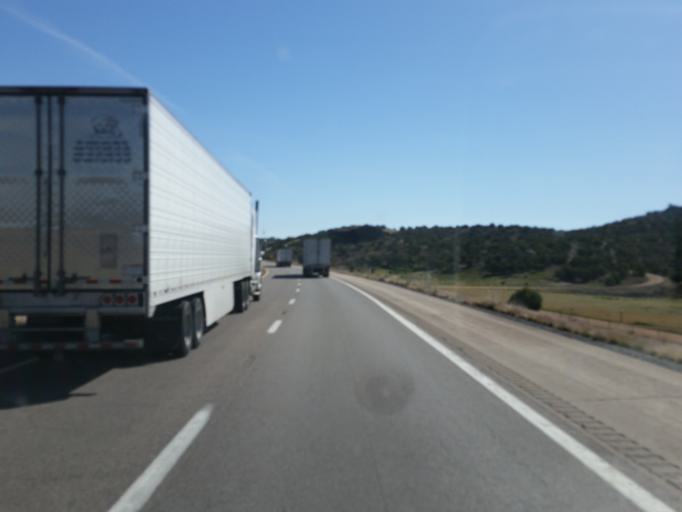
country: US
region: Arizona
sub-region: Mohave County
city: Peach Springs
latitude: 35.1836
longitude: -113.4508
